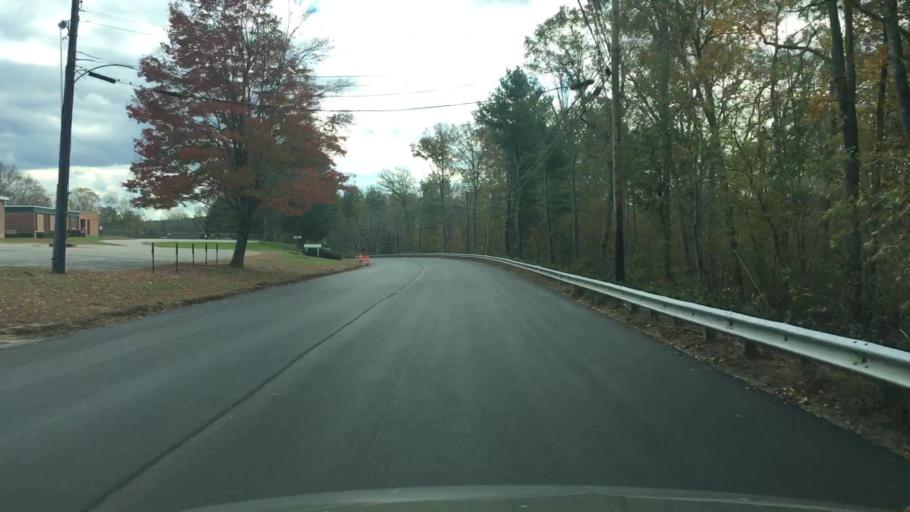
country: US
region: Connecticut
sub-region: Tolland County
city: Storrs
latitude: 41.8933
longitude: -72.1702
